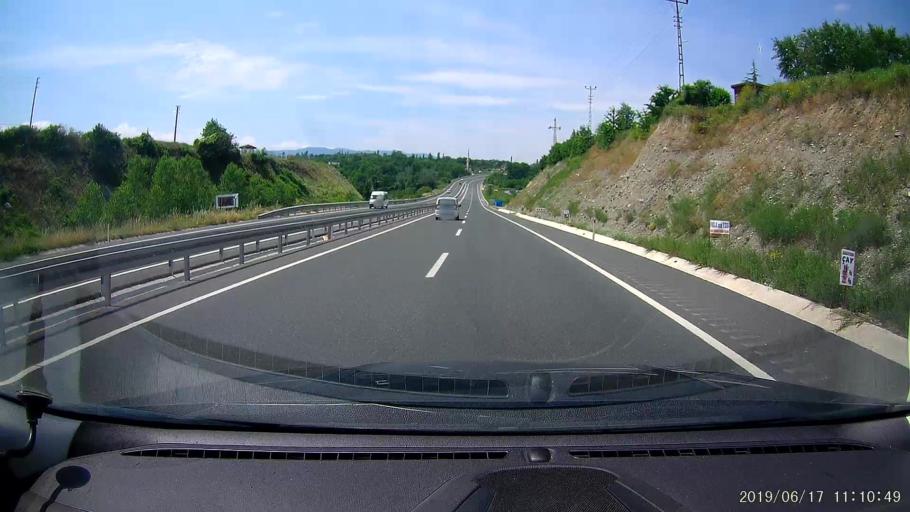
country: TR
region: Kastamonu
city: Tosya
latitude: 40.9949
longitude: 34.0178
